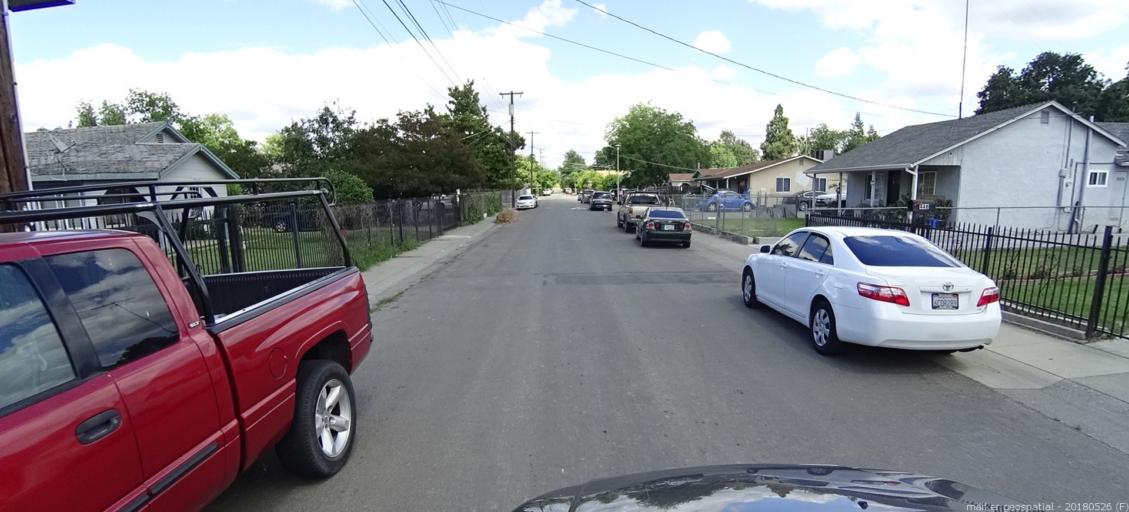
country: US
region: California
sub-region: Sacramento County
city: Sacramento
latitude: 38.6140
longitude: -121.4734
